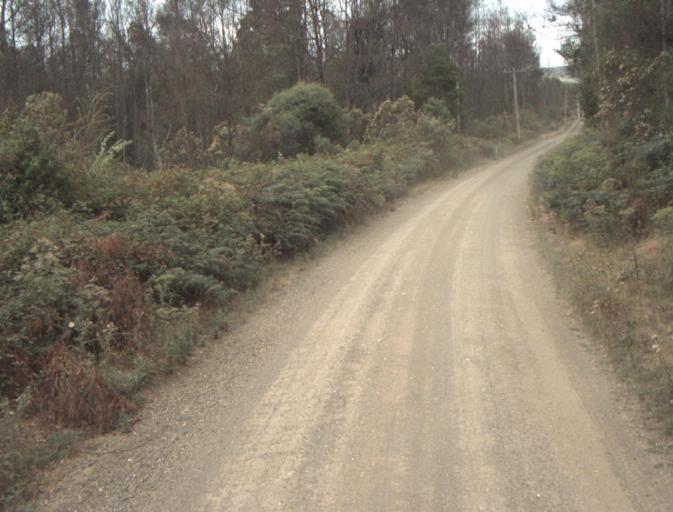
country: AU
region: Tasmania
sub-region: Dorset
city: Bridport
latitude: -41.1936
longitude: 147.2632
